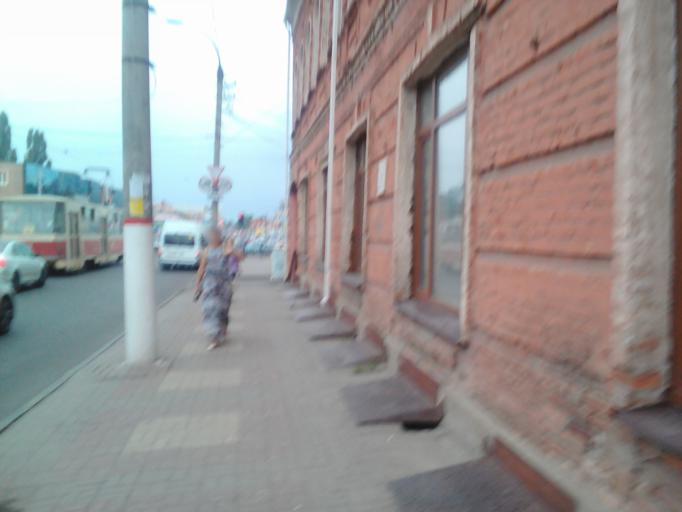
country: RU
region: Kursk
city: Kursk
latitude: 51.7264
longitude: 36.1852
